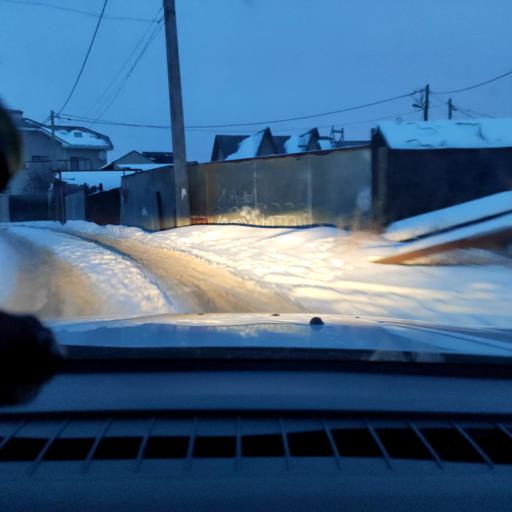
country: RU
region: Samara
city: Samara
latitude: 53.2267
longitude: 50.1592
